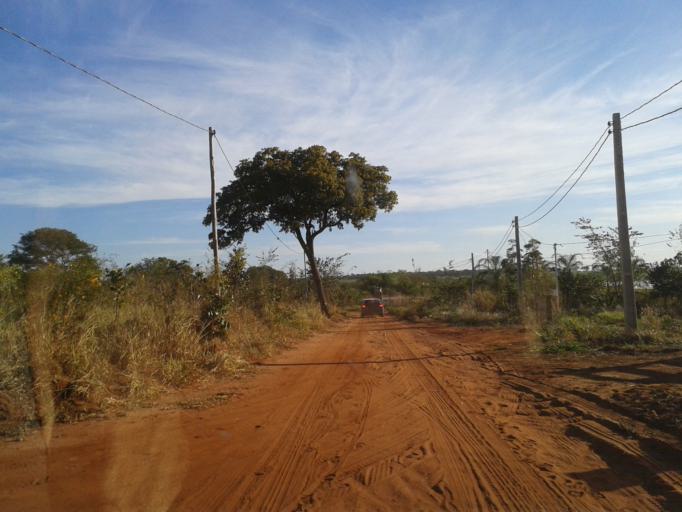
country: BR
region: Minas Gerais
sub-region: Santa Vitoria
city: Santa Vitoria
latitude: -18.9984
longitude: -50.3803
